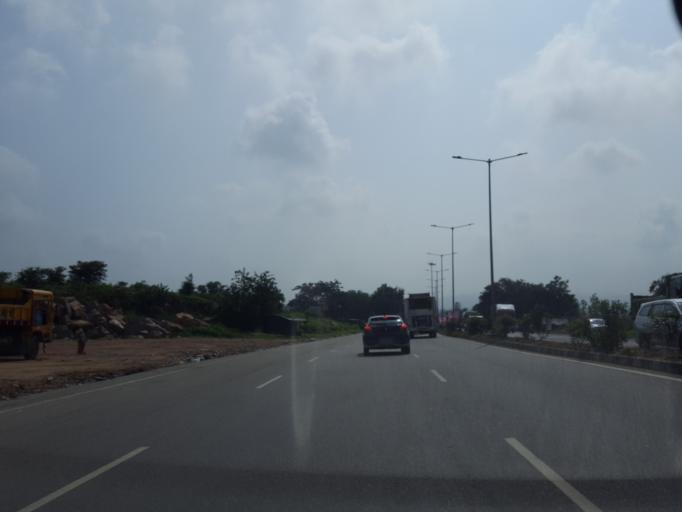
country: IN
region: Telangana
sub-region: Rangareddi
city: Lal Bahadur Nagar
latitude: 17.3157
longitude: 78.6726
